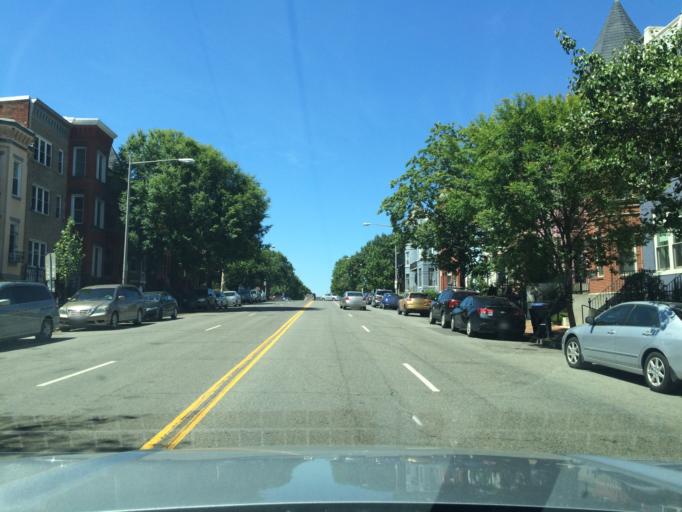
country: US
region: Washington, D.C.
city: Washington, D.C.
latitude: 38.9047
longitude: -77.0199
